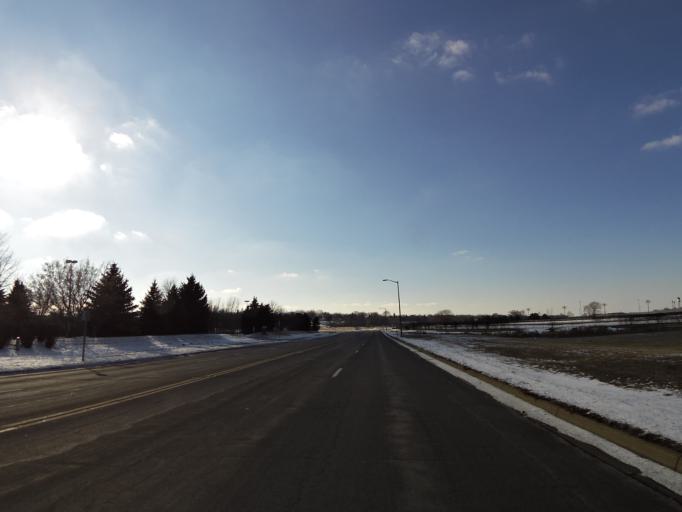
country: US
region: Minnesota
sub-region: Scott County
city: Shakopee
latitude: 44.7851
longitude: -93.4767
